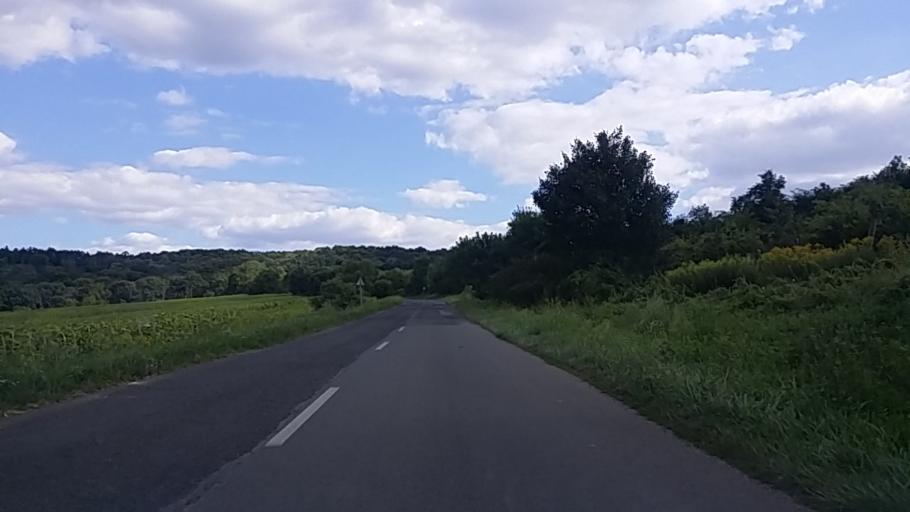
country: HU
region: Baranya
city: Sasd
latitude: 46.1597
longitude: 18.0931
